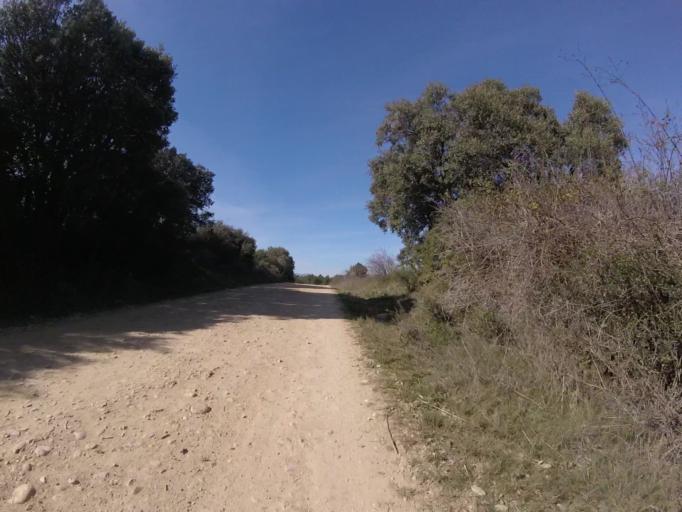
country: ES
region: Navarre
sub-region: Provincia de Navarra
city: Oteiza
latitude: 42.6423
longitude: -1.9555
